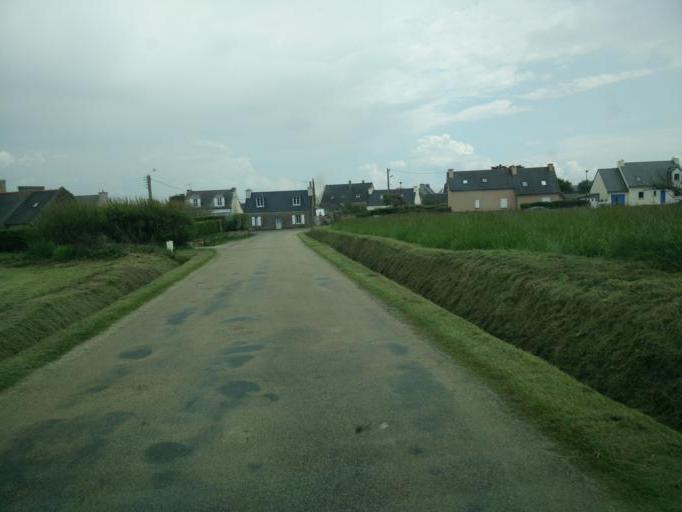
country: FR
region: Brittany
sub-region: Departement du Finistere
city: Camaret-sur-Mer
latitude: 48.2739
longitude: -4.6087
